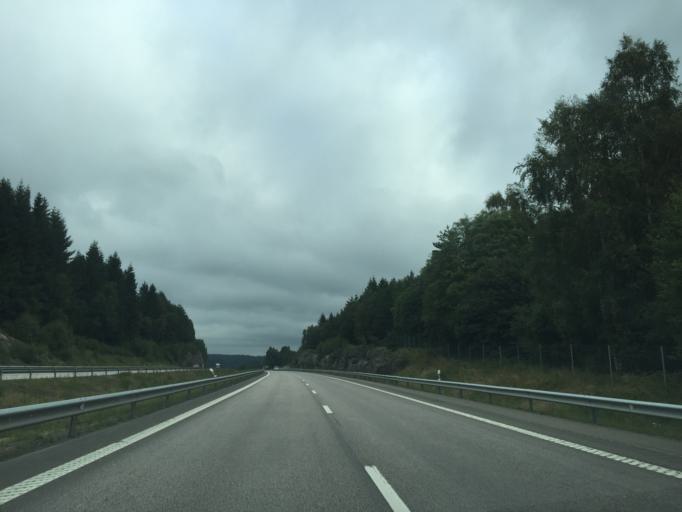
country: SE
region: Halland
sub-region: Kungsbacka Kommun
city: Frillesas
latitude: 57.3517
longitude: 12.2100
